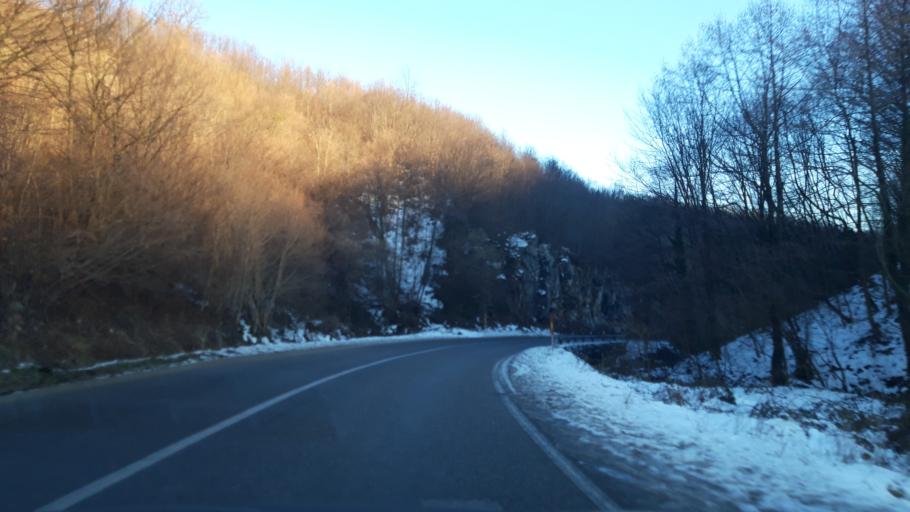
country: BA
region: Republika Srpska
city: Vlasenica
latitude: 44.1846
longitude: 18.9719
